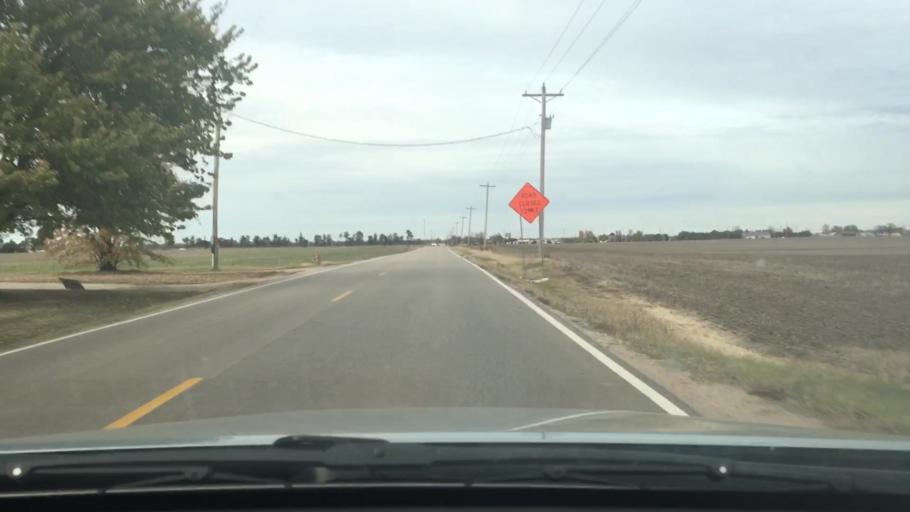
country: US
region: Kansas
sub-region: Sedgwick County
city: Maize
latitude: 37.7729
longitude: -97.4994
